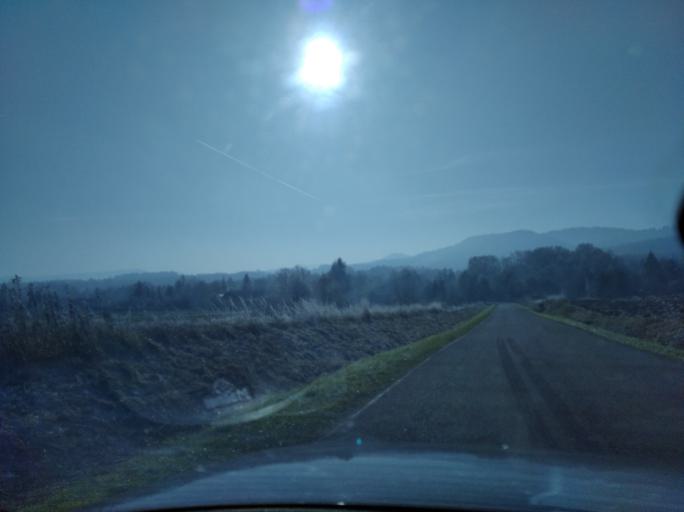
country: PL
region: Subcarpathian Voivodeship
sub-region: Powiat strzyzowski
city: Wysoka Strzyzowska
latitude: 49.8367
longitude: 21.7131
